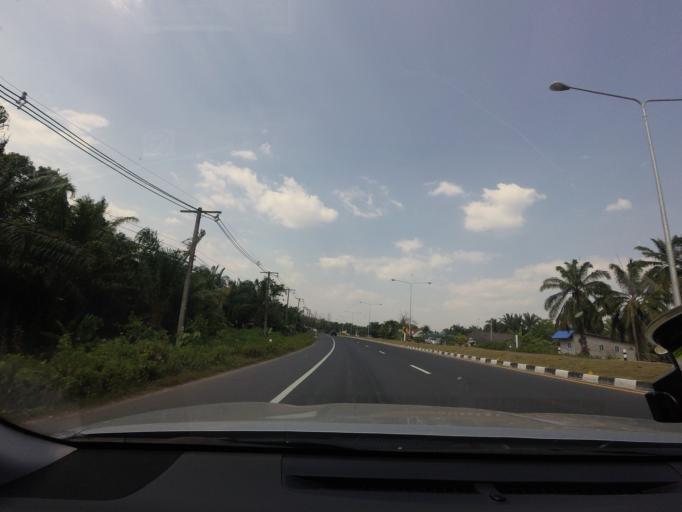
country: TH
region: Phangnga
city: Thap Put
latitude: 8.5657
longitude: 98.7371
